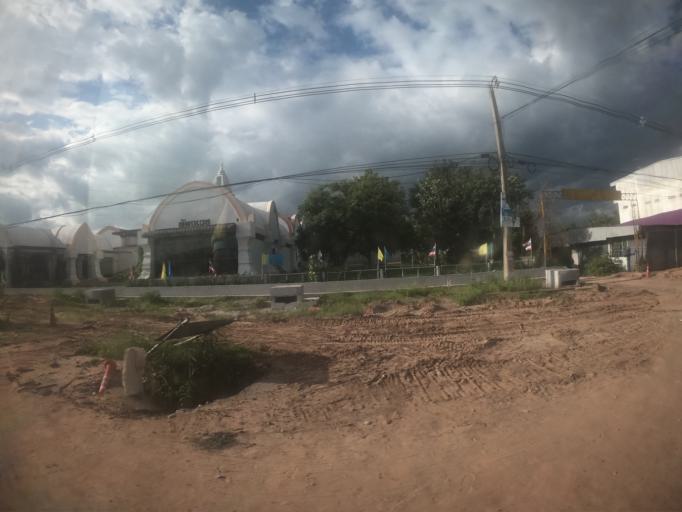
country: TH
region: Surin
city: Kap Choeng
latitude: 14.4765
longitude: 103.5924
